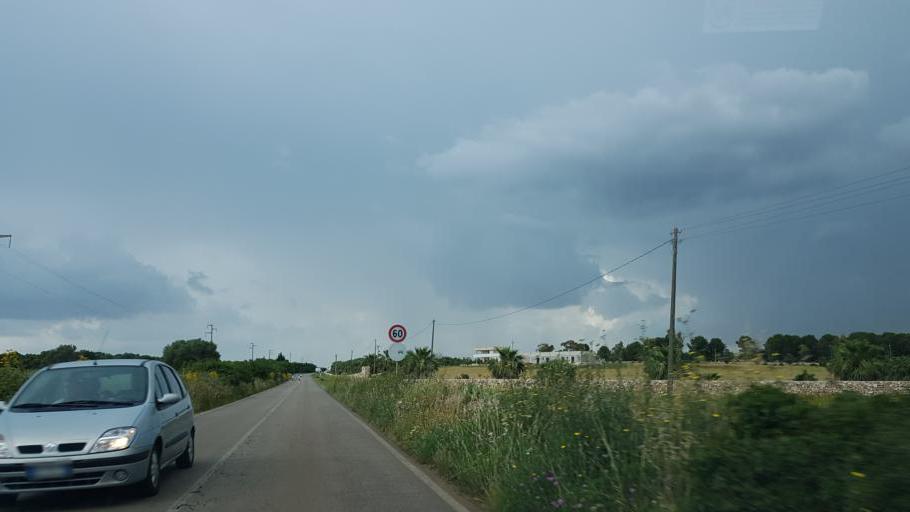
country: IT
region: Apulia
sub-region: Provincia di Lecce
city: Porto Cesareo
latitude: 40.3228
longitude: 17.8559
